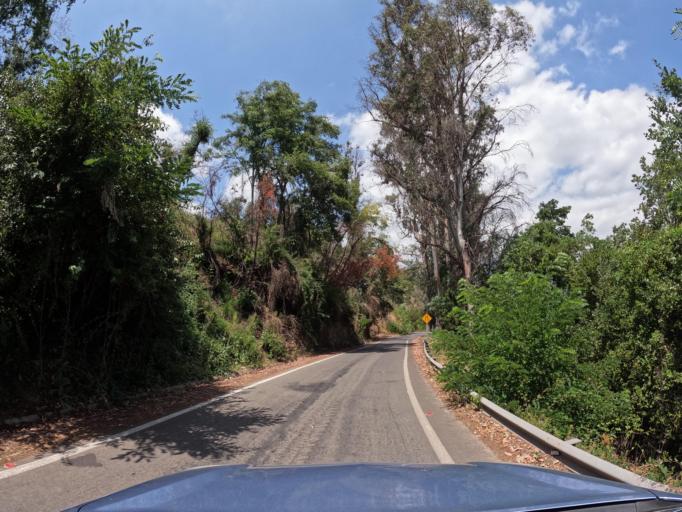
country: CL
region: Maule
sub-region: Provincia de Curico
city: Molina
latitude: -35.1760
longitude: -71.0924
